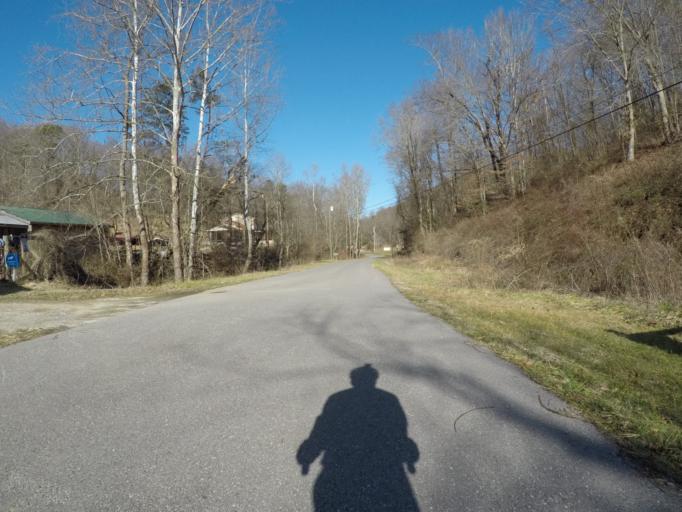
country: US
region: Kentucky
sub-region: Boyd County
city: Catlettsburg
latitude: 38.4126
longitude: -82.6109
